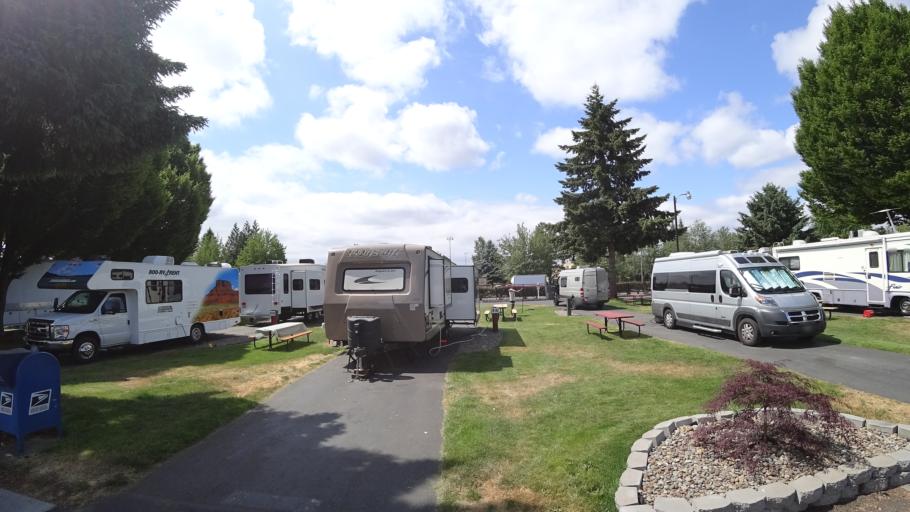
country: US
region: Washington
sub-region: Clark County
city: Vancouver
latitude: 45.6161
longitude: -122.6862
